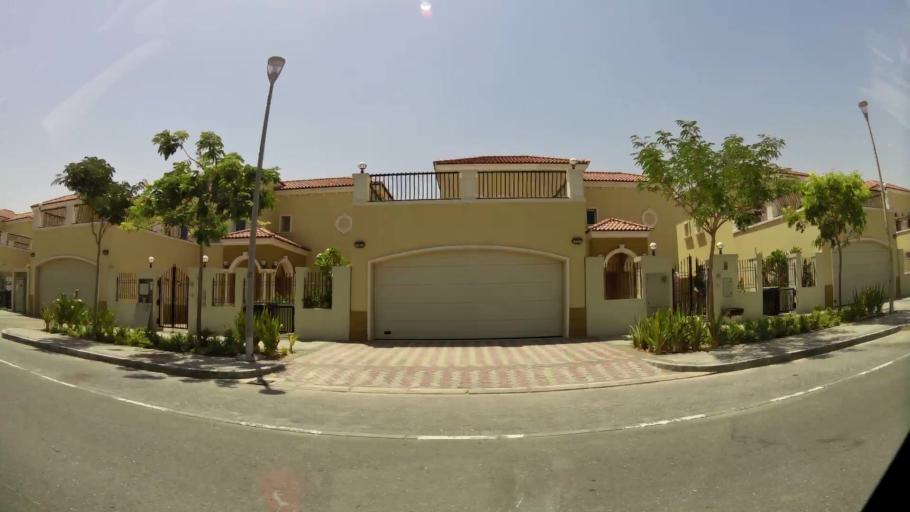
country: AE
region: Dubai
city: Dubai
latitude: 25.0361
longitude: 55.1681
